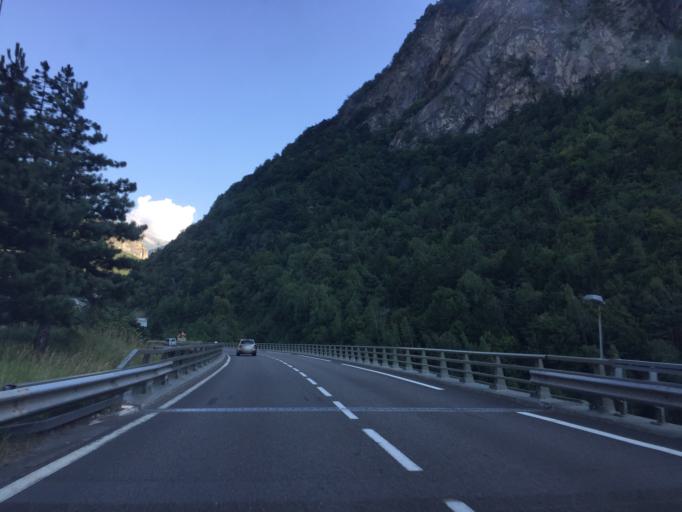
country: FR
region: Rhone-Alpes
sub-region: Departement de la Savoie
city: Moutiers
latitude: 45.4884
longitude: 6.5197
